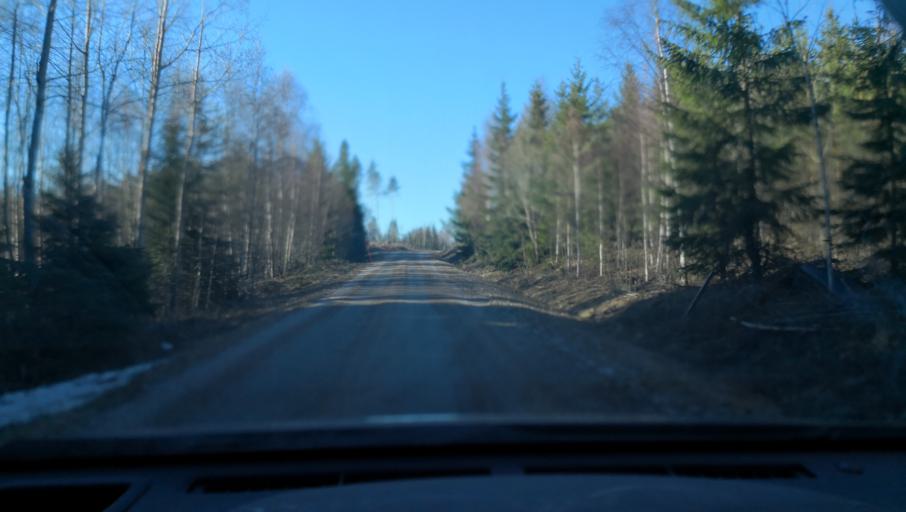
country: SE
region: Vaestmanland
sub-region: Sala Kommun
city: Sala
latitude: 60.1579
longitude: 16.6297
